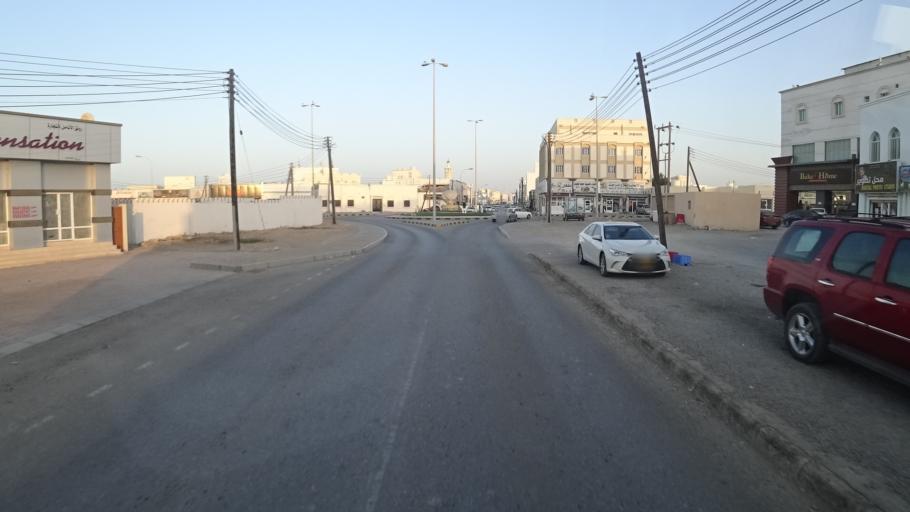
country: OM
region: Ash Sharqiyah
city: Sur
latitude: 22.5816
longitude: 59.5071
